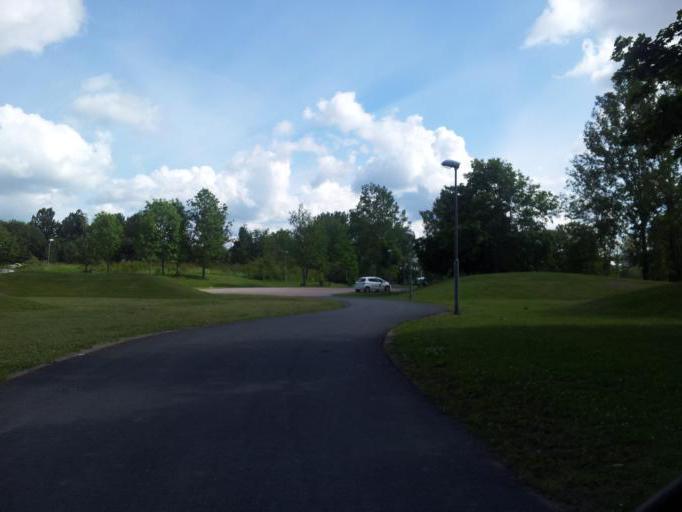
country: SE
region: Uppsala
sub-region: Uppsala Kommun
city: Uppsala
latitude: 59.8769
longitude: 17.6610
